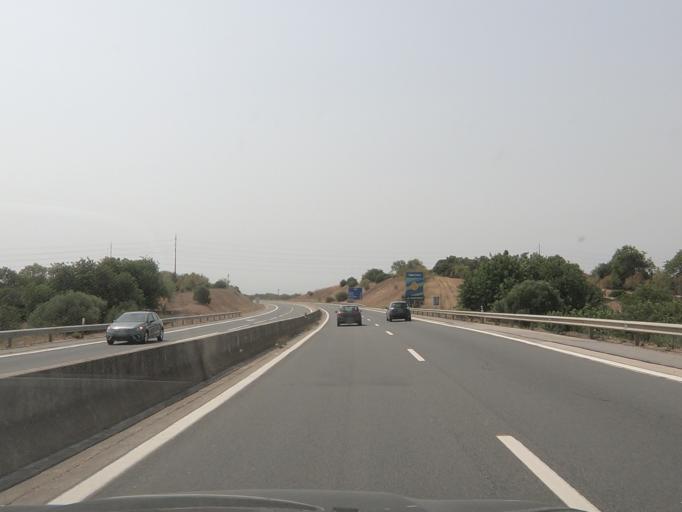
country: PT
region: Faro
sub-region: Albufeira
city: Ferreiras
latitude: 37.1382
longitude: -8.2606
